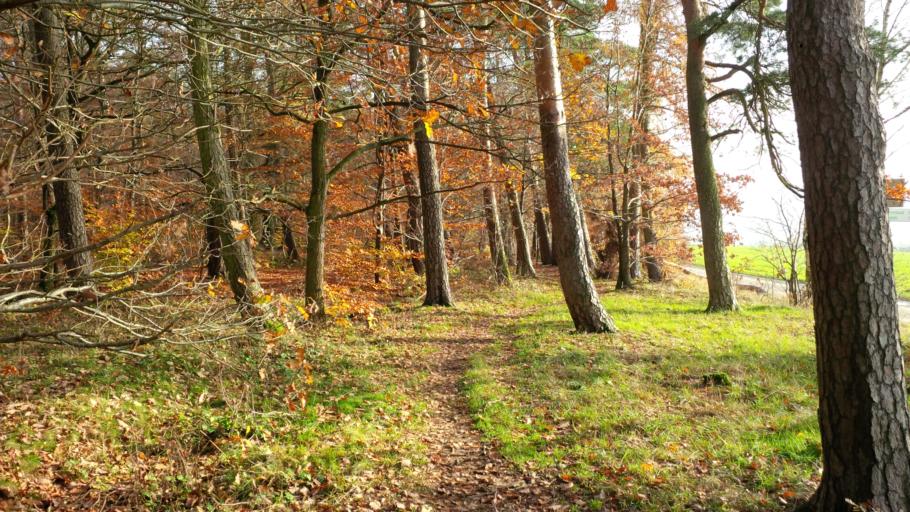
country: DE
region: Hesse
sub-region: Regierungsbezirk Darmstadt
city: Wehrheim
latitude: 50.3120
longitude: 8.5803
